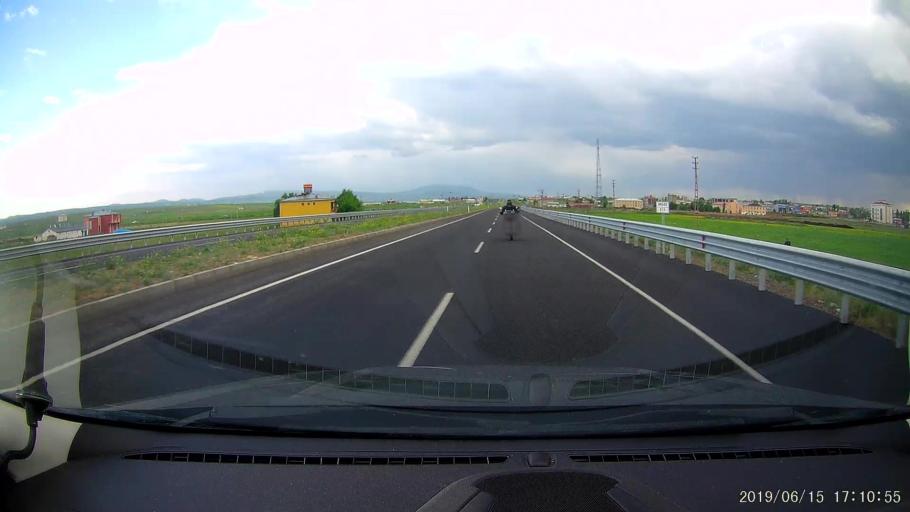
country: TR
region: Kars
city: Kars
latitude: 40.6168
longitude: 43.1333
